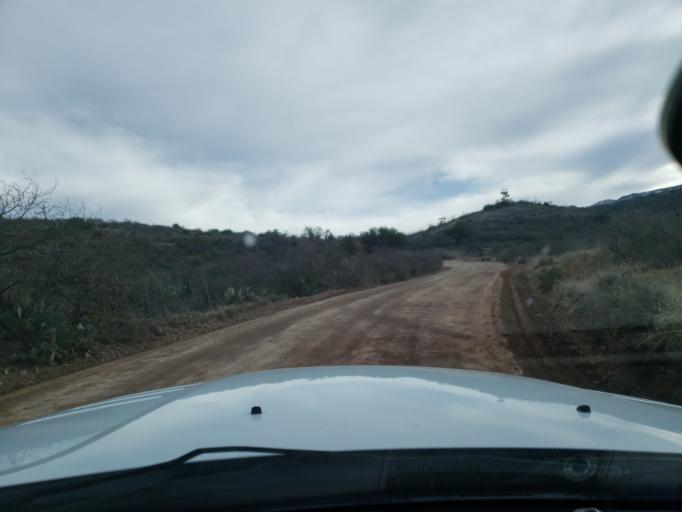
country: US
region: Arizona
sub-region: Pinal County
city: Oracle
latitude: 32.5507
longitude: -110.7079
